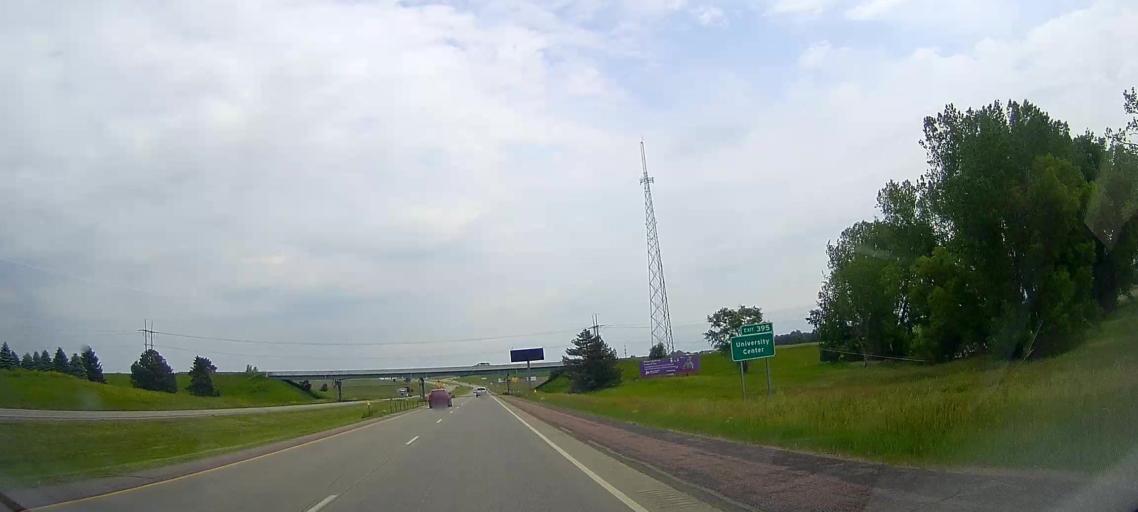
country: US
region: South Dakota
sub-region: Minnehaha County
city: Crooks
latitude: 43.6087
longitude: -96.8125
